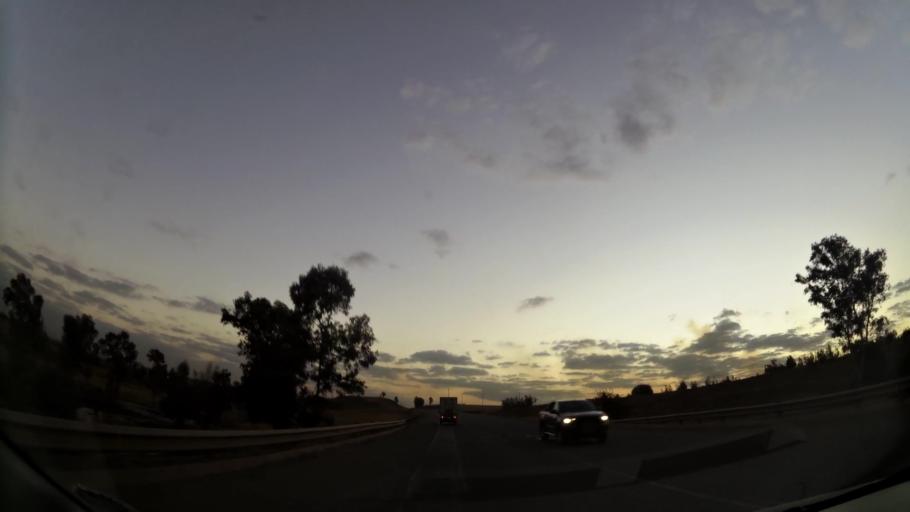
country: ZA
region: Gauteng
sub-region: West Rand District Municipality
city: Randfontein
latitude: -26.0735
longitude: 27.6542
